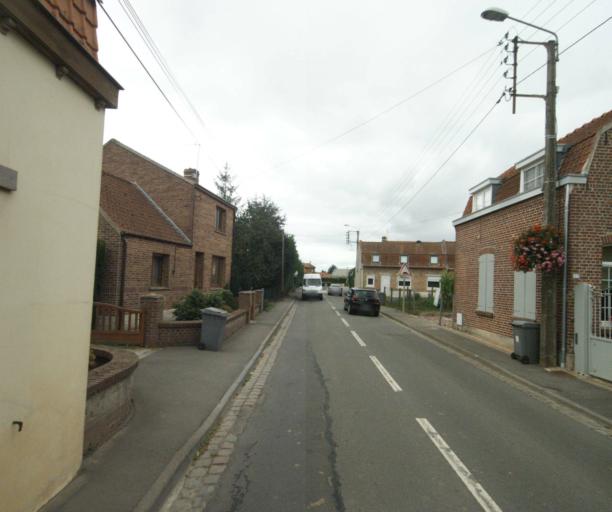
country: FR
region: Nord-Pas-de-Calais
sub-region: Departement du Nord
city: Fretin
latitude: 50.5543
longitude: 3.1389
